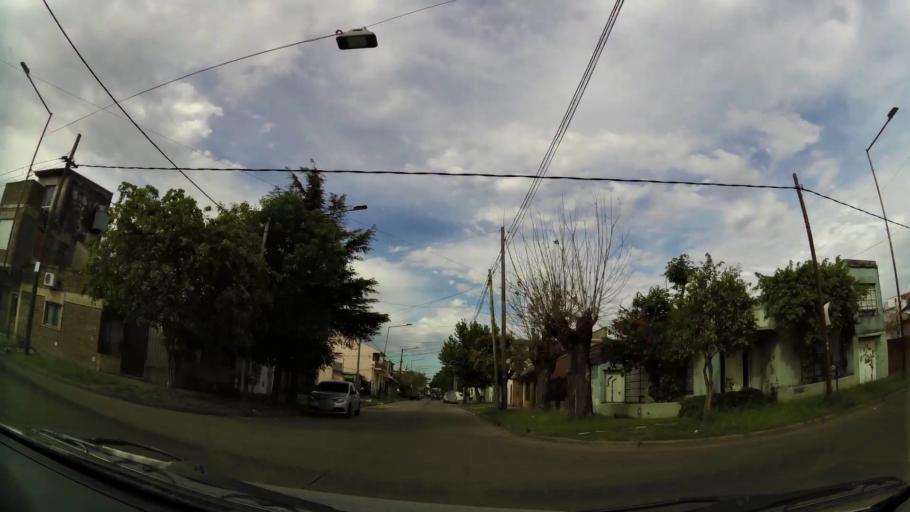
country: AR
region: Buenos Aires
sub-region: Partido de Lanus
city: Lanus
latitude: -34.6978
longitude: -58.3799
